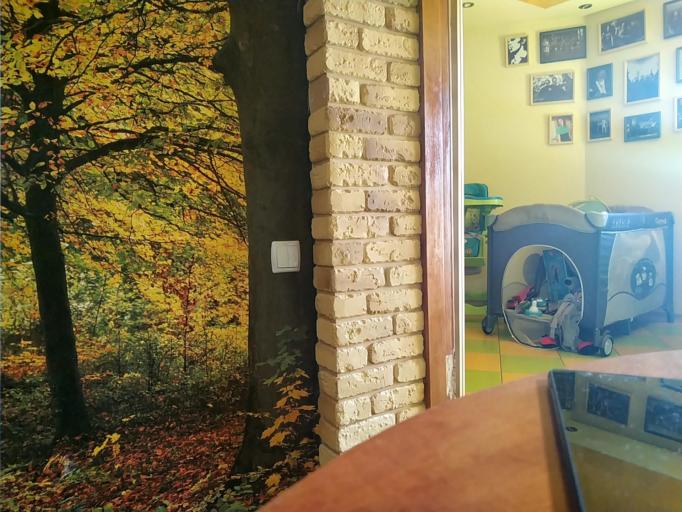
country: RU
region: Tverskaya
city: Vyshniy Volochek
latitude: 57.4924
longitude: 34.6686
